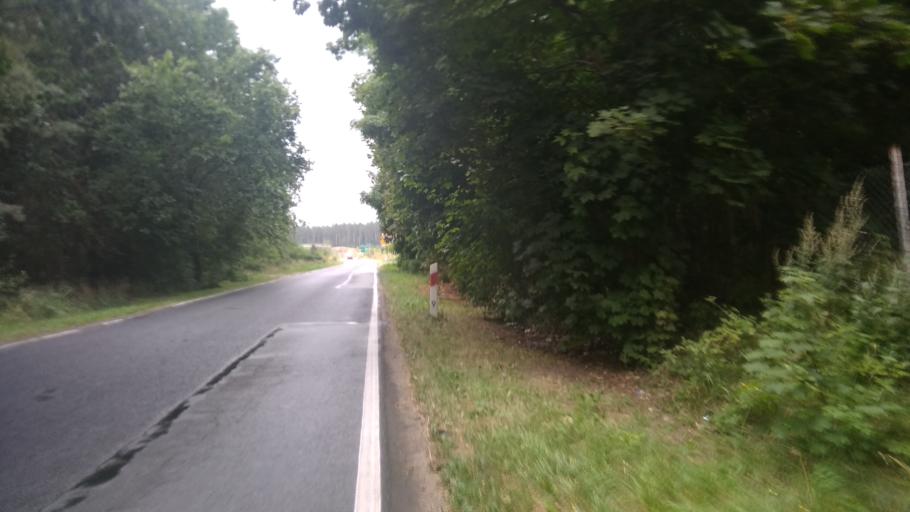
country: PL
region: Kujawsko-Pomorskie
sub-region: Powiat bydgoski
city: Osielsko
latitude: 53.2205
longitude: 18.1330
